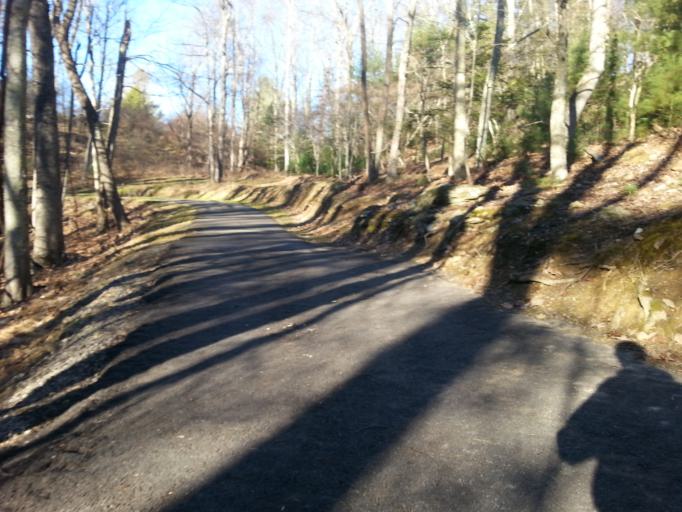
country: US
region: West Virginia
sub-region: Mercer County
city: Athens
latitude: 37.5388
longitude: -80.9824
